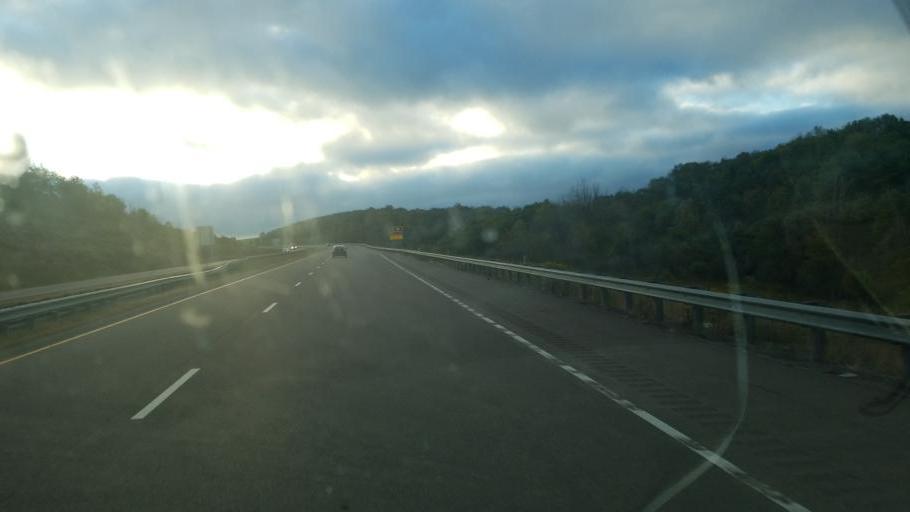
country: US
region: Maryland
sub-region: Allegany County
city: Frostburg
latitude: 39.6827
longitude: -79.0508
